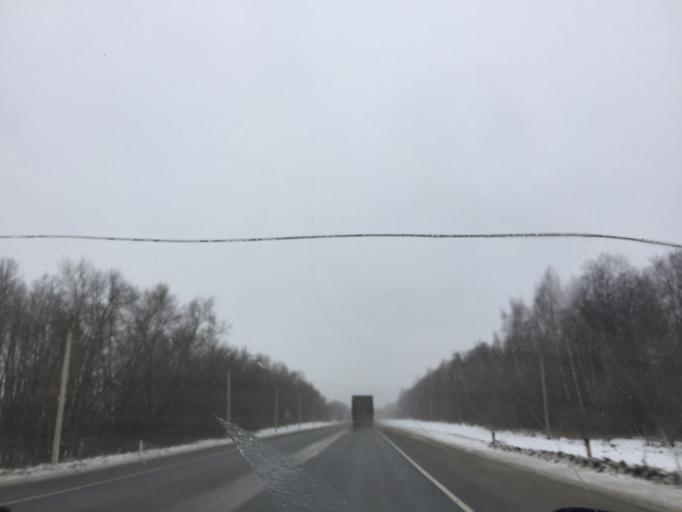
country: RU
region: Tula
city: Plavsk
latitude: 53.7501
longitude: 37.3271
